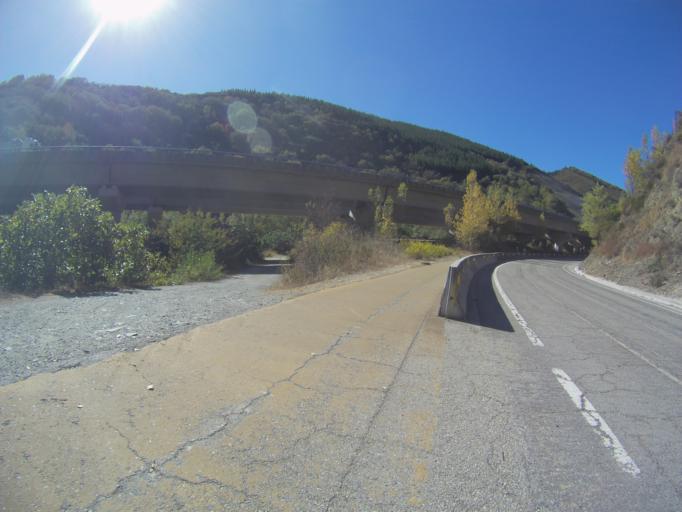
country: ES
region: Castille and Leon
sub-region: Provincia de Leon
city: Villafranca del Bierzo
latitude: 42.6148
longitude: -6.8233
